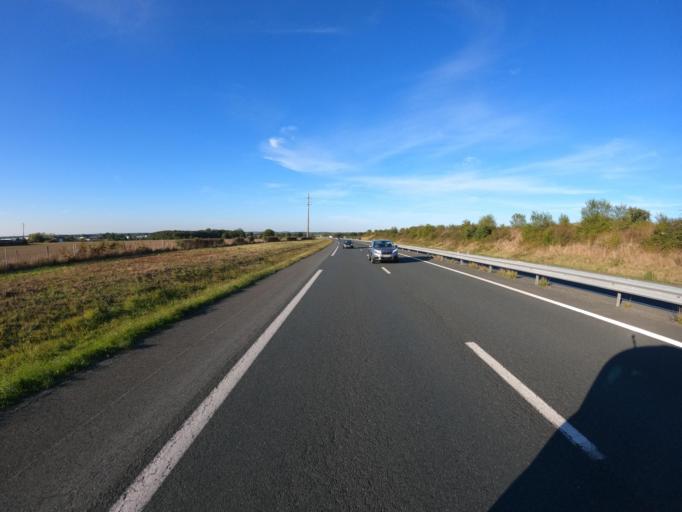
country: FR
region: Pays de la Loire
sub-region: Departement de Maine-et-Loire
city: Mazieres-en-Mauges
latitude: 47.0657
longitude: -0.8270
